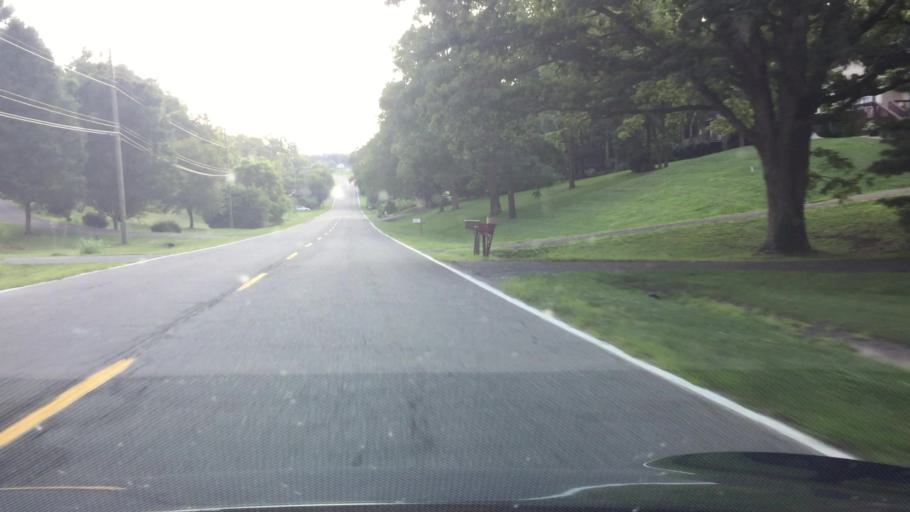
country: US
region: Virginia
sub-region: Pulaski County
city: Pulaski
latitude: 36.9566
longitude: -80.8688
